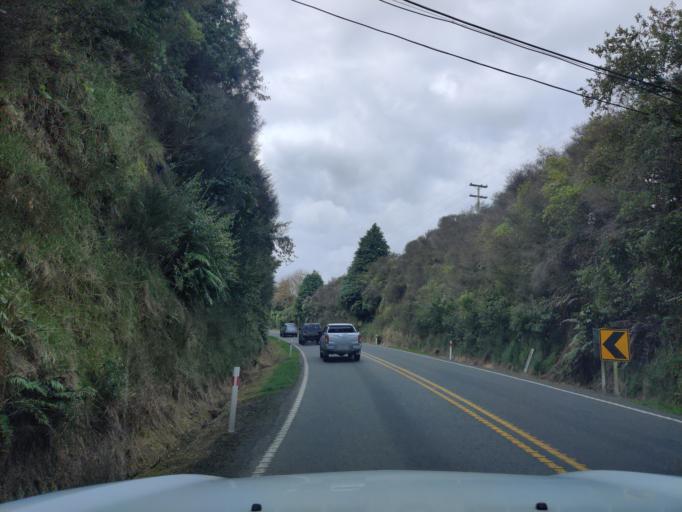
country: NZ
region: Manawatu-Wanganui
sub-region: Ruapehu District
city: Waiouru
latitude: -39.5336
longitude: 175.3047
